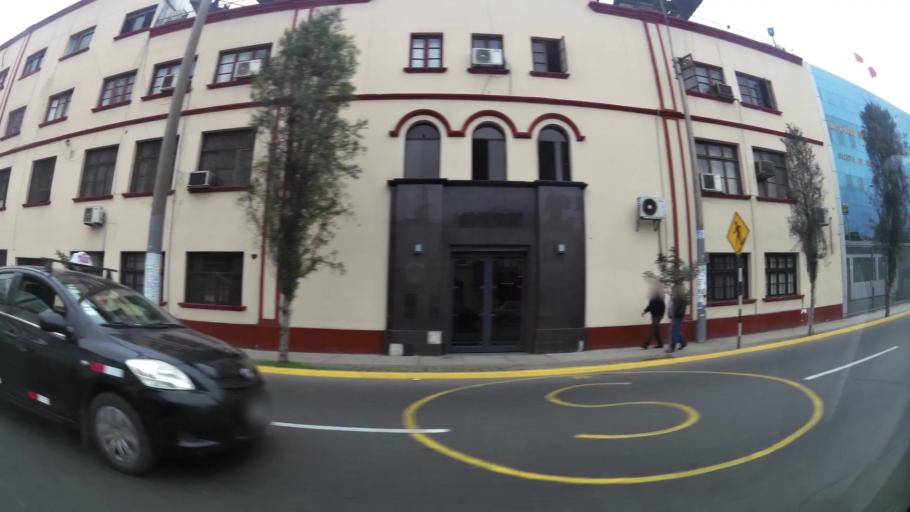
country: PE
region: Lima
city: Lima
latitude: -12.0664
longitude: -77.0360
